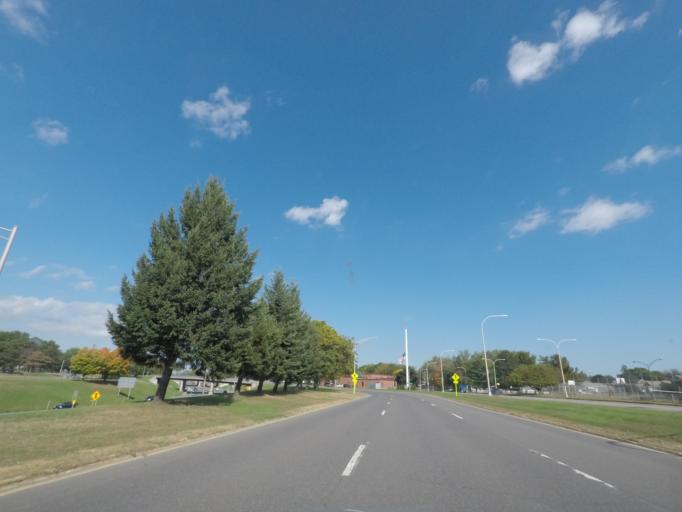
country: US
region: New York
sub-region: Albany County
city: Roessleville
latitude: 42.6757
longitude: -73.8026
